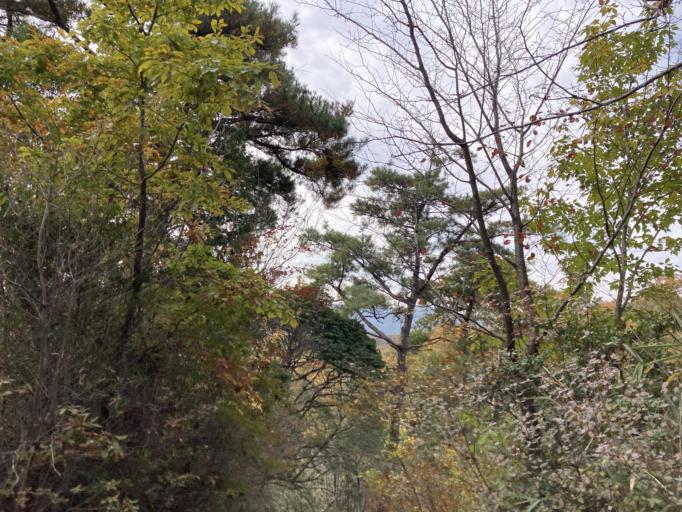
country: JP
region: Osaka
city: Hirakata
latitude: 34.7652
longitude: 135.7068
